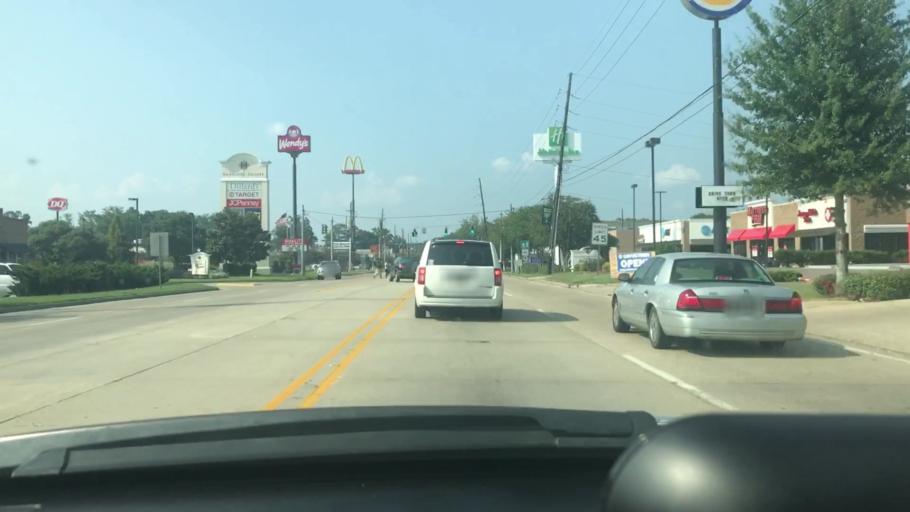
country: US
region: Louisiana
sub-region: Tangipahoa Parish
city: Hammond
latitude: 30.4826
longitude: -90.4569
